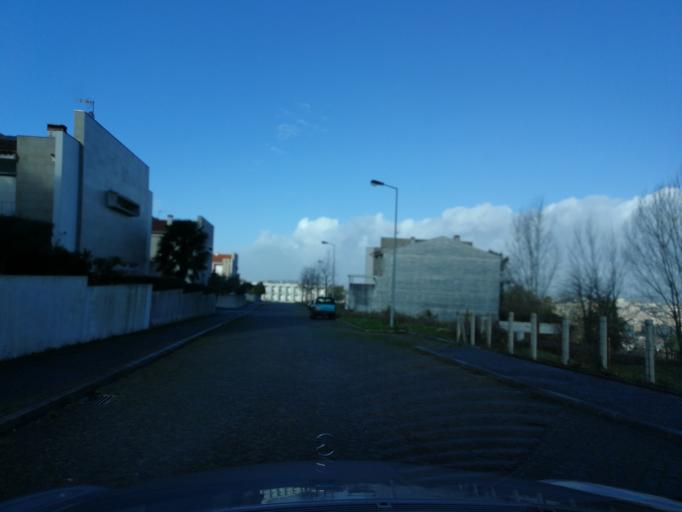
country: PT
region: Braga
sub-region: Braga
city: Braga
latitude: 41.5379
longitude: -8.3912
